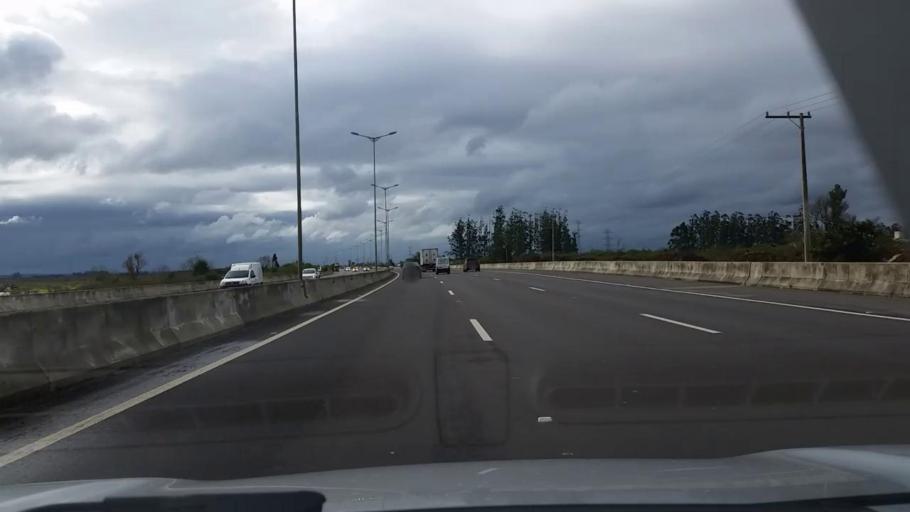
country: BR
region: Rio Grande do Sul
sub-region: Canoas
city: Canoas
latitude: -29.9592
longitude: -51.2025
